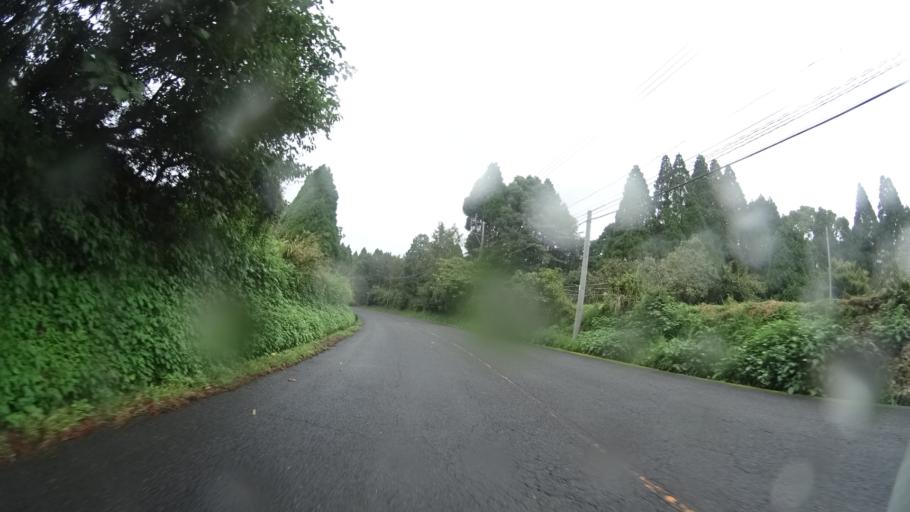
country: JP
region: Kagoshima
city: Kajiki
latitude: 31.7909
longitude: 130.6758
